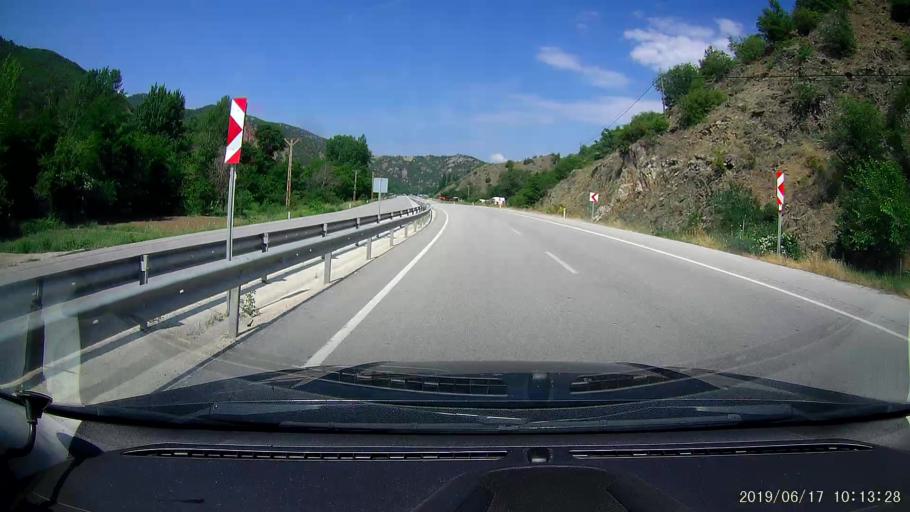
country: TR
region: Amasya
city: Saraycik
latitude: 40.9869
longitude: 35.0482
